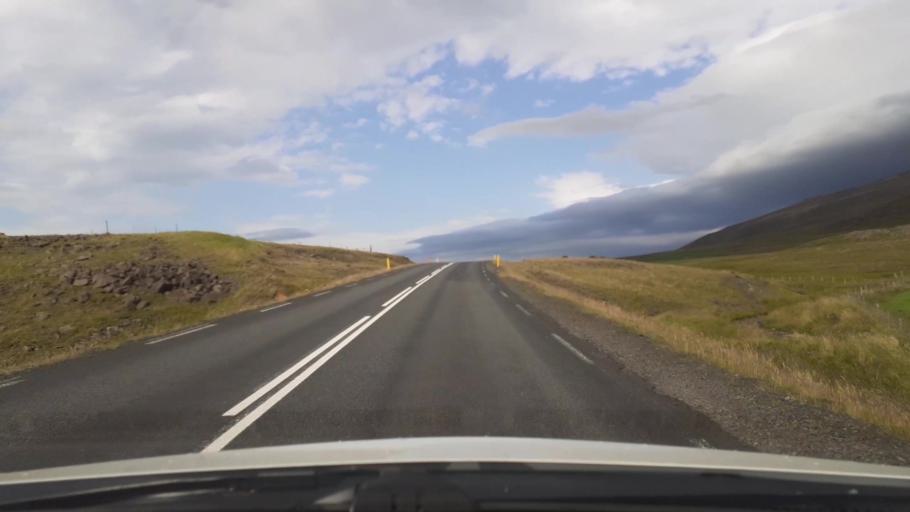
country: IS
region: Capital Region
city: Mosfellsbaer
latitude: 64.3975
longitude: -21.5172
